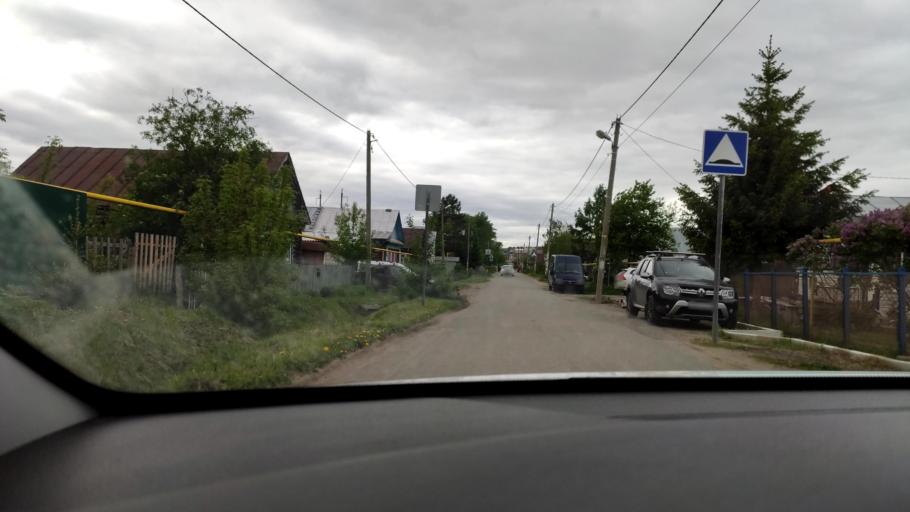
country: RU
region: Tatarstan
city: Stolbishchi
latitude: 55.7484
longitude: 49.3016
